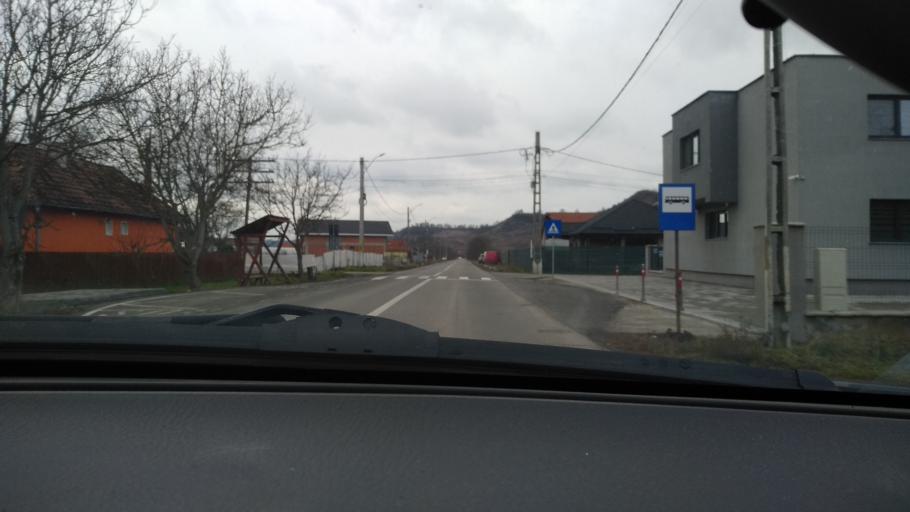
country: RO
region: Mures
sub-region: Comuna Livezeni
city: Livezeni
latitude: 46.5415
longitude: 24.6757
